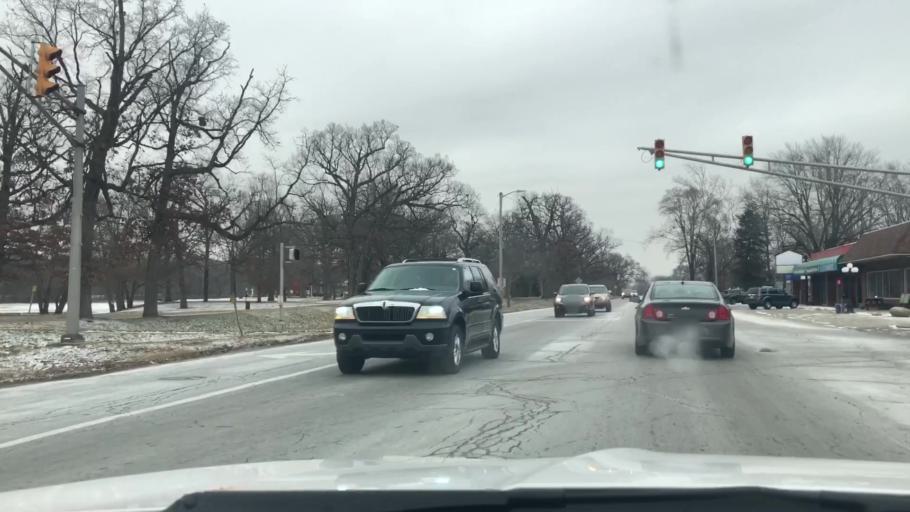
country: US
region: Indiana
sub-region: Fulton County
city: Rochester
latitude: 41.0641
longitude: -86.2054
